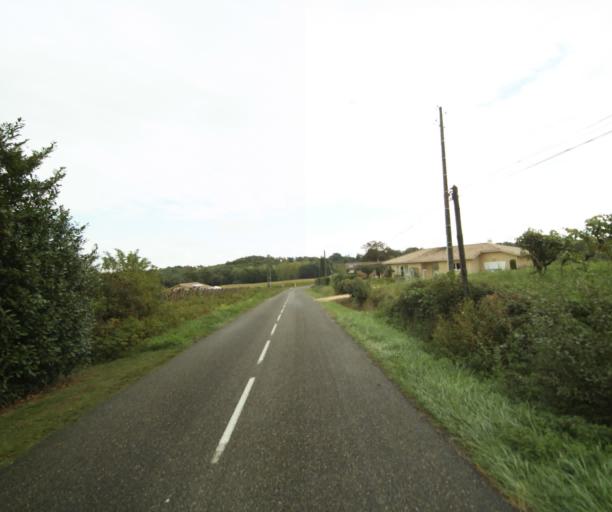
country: FR
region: Midi-Pyrenees
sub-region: Departement du Gers
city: Cazaubon
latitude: 43.8666
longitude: -0.0558
